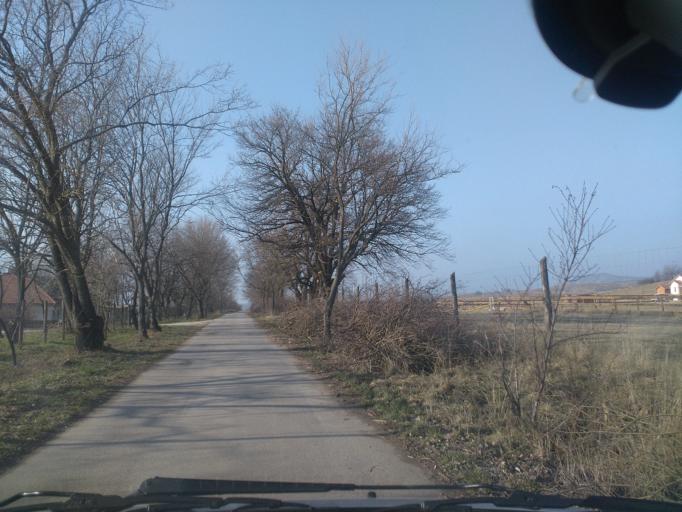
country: HU
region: Komarom-Esztergom
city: Piliscsev
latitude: 47.6857
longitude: 18.8080
